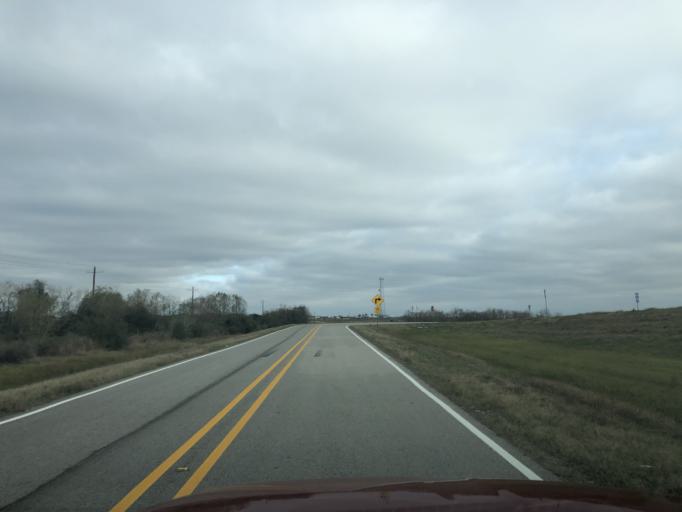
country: US
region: Texas
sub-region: Chambers County
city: Winnie
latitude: 29.8312
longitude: -94.4828
